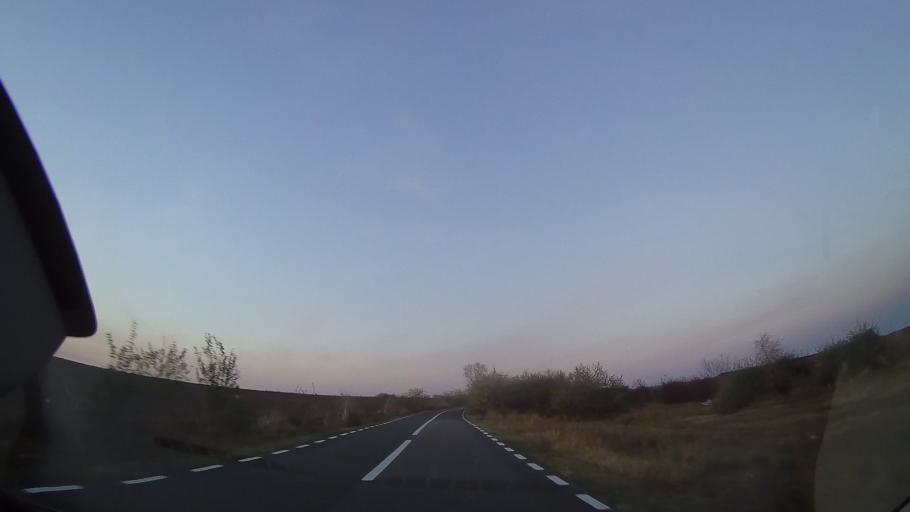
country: RO
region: Constanta
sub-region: Comuna Cobadin
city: Cobadin
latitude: 44.0305
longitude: 28.2614
